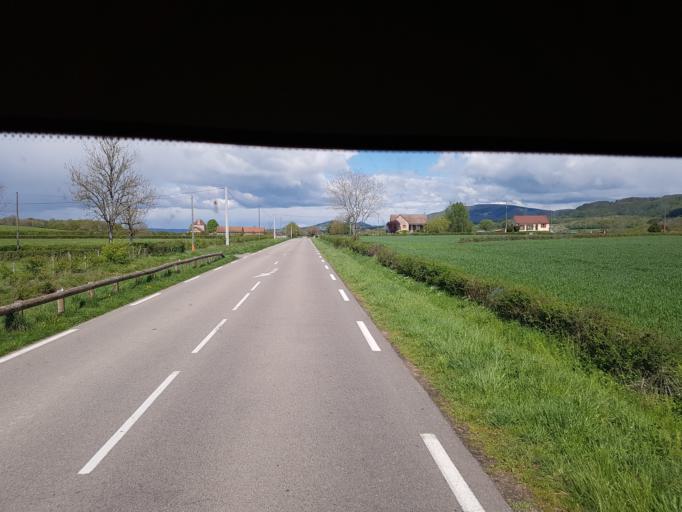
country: FR
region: Bourgogne
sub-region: Departement de Saone-et-Loire
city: Etang-sur-Arroux
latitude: 46.8786
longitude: 4.1799
